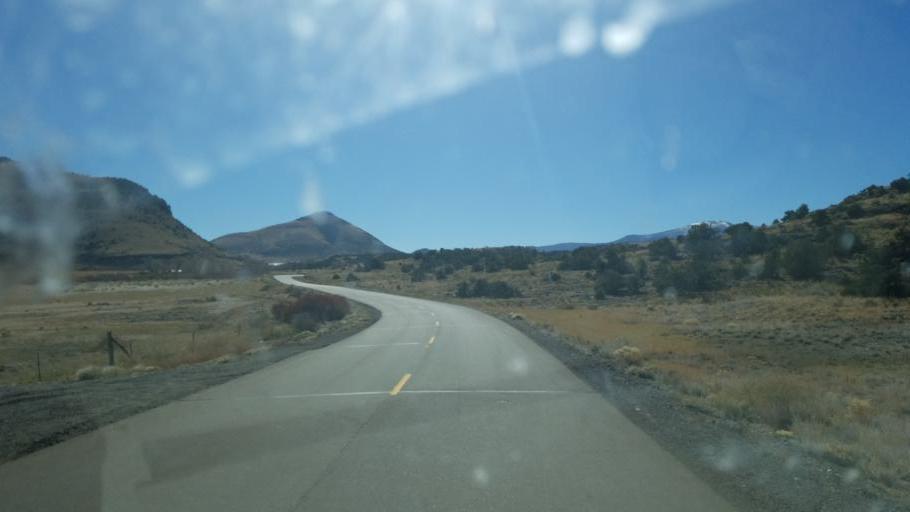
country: US
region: Colorado
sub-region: Rio Grande County
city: Del Norte
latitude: 37.6471
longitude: -106.3649
